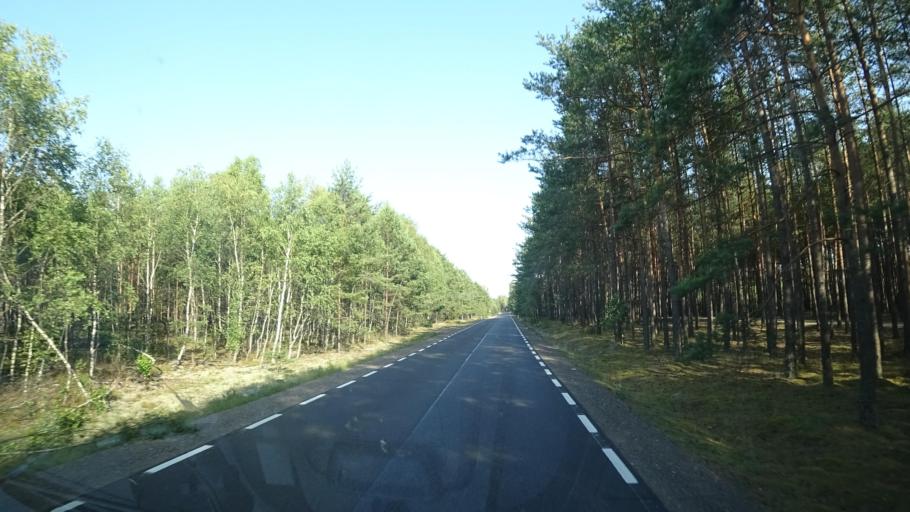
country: PL
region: Pomeranian Voivodeship
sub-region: Powiat chojnicki
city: Chojnice
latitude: 53.8585
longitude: 17.5370
